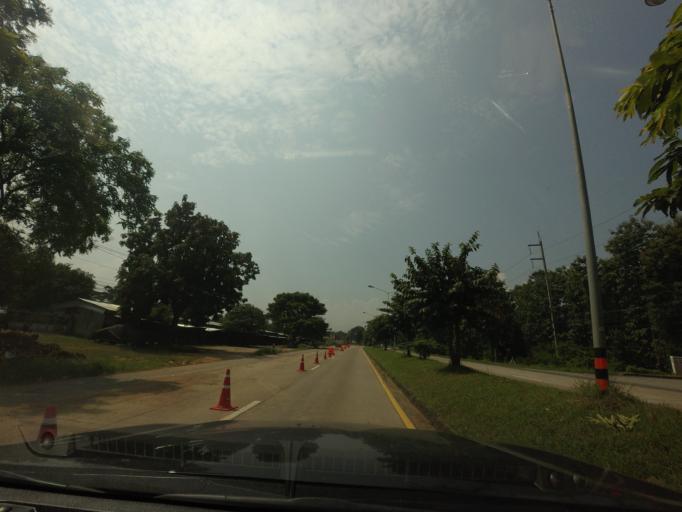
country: TH
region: Phrae
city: Den Chai
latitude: 17.9794
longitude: 100.0907
